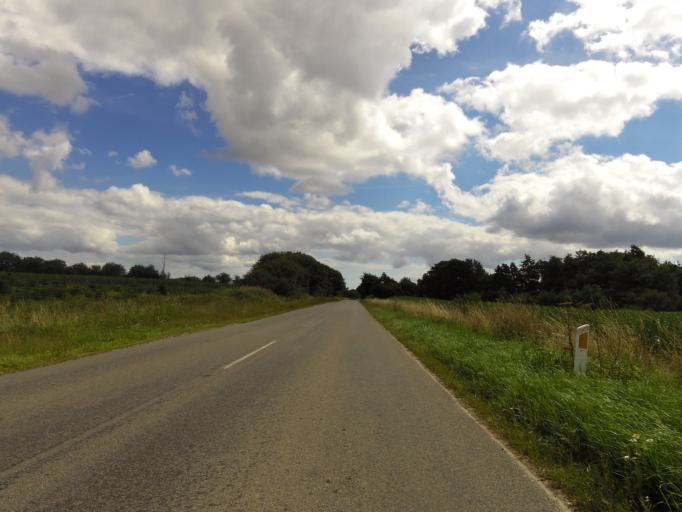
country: DK
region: South Denmark
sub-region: Haderslev Kommune
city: Haderslev
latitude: 55.2788
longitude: 9.4120
